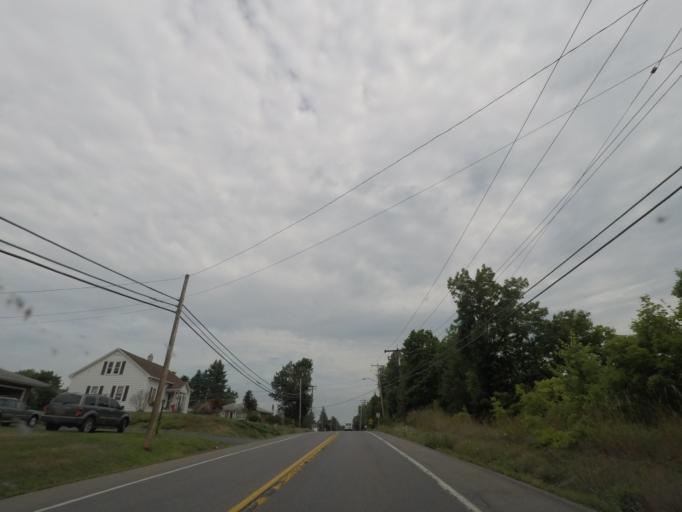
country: US
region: New York
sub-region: Saratoga County
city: Waterford
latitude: 42.7970
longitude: -73.6801
